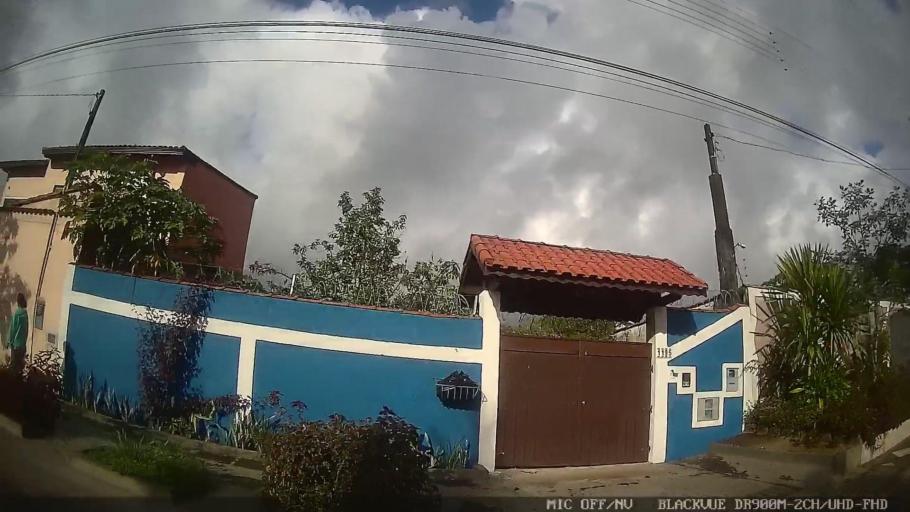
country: BR
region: Sao Paulo
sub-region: Itanhaem
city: Itanhaem
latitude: -24.1918
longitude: -46.8636
